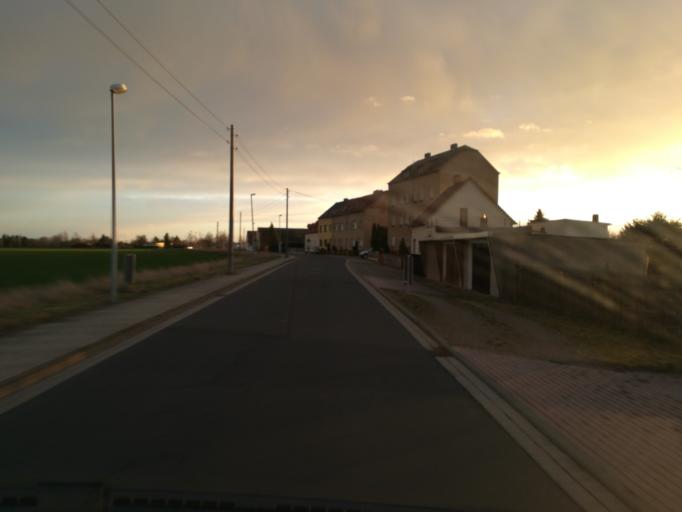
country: DE
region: Saxony
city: Wiedemar
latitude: 51.5070
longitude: 12.2275
